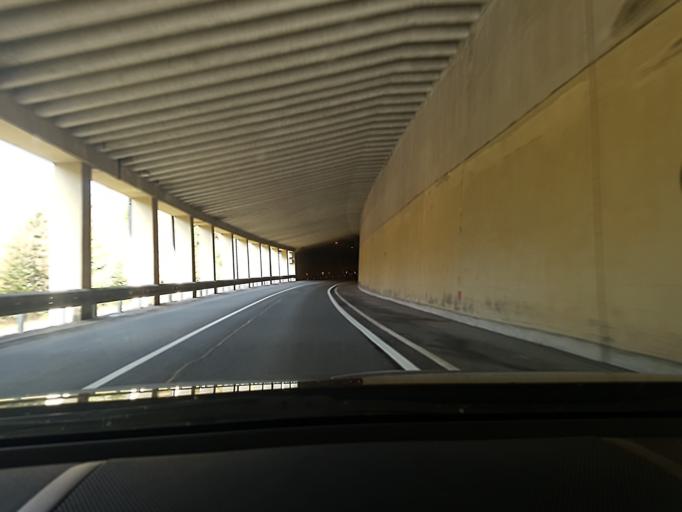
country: AT
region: Salzburg
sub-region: Politischer Bezirk Tamsweg
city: Tweng
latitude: 47.2040
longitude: 13.5864
